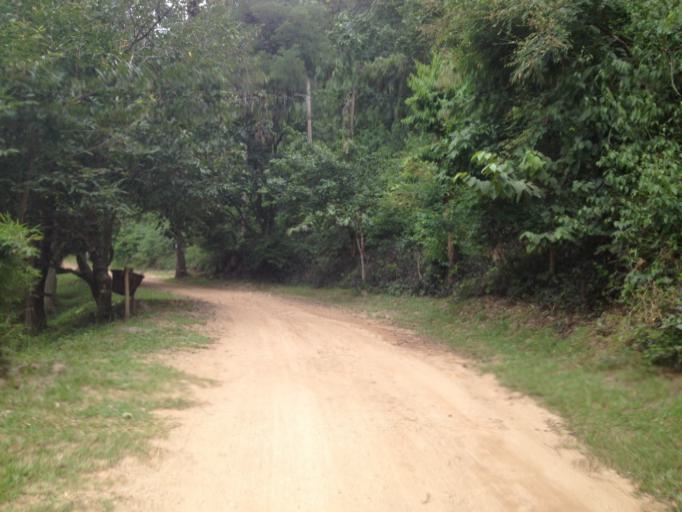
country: TH
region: Chiang Mai
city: Hang Dong
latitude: 18.7213
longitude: 98.8229
